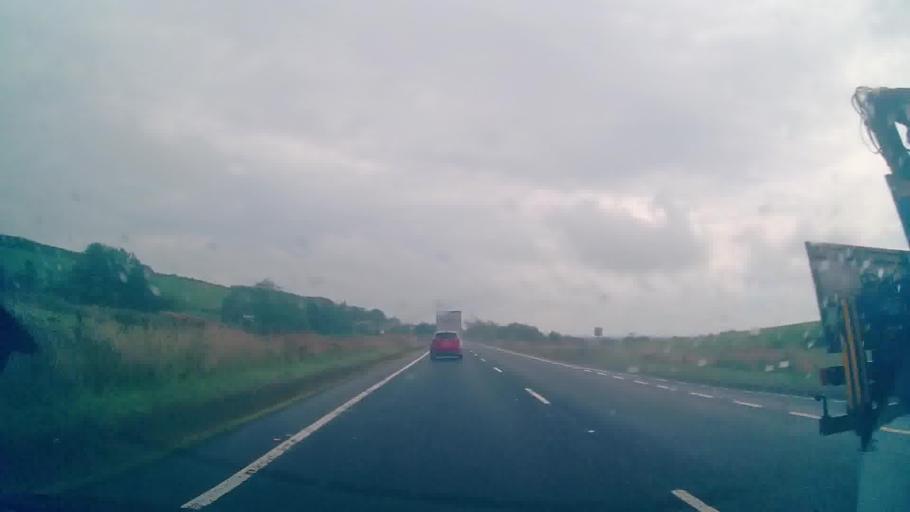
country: GB
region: Scotland
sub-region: Dumfries and Galloway
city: Lochmaben
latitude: 55.0388
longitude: -3.4357
